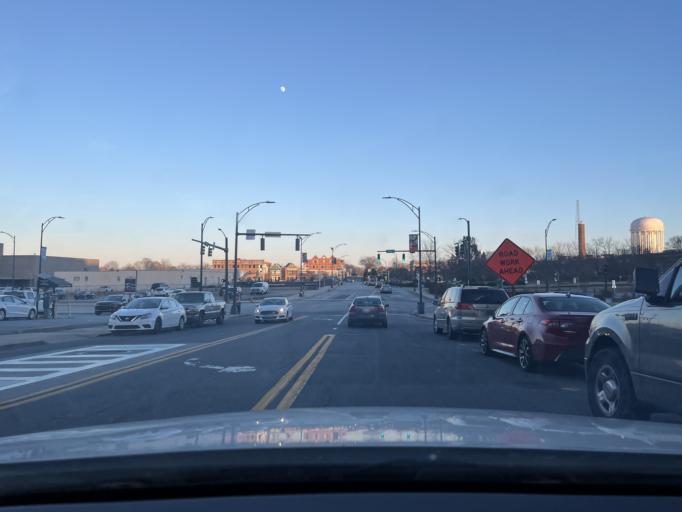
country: US
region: North Carolina
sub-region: Guilford County
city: Greensboro
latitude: 36.0702
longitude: -79.7899
